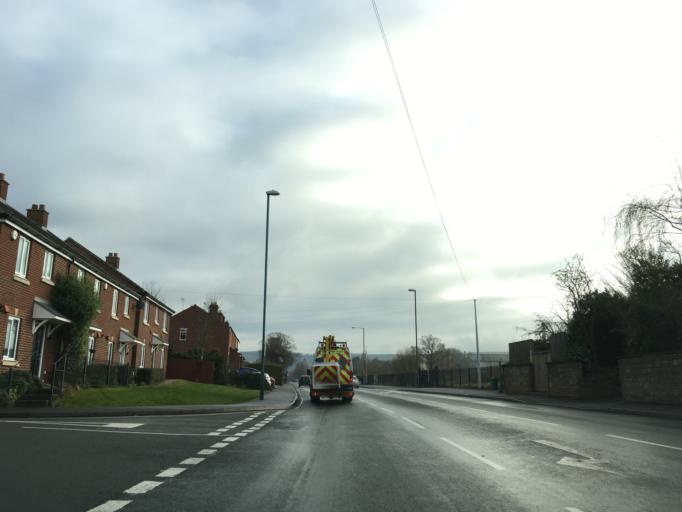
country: GB
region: England
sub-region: Gloucestershire
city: Churchdown
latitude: 51.8499
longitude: -2.1710
